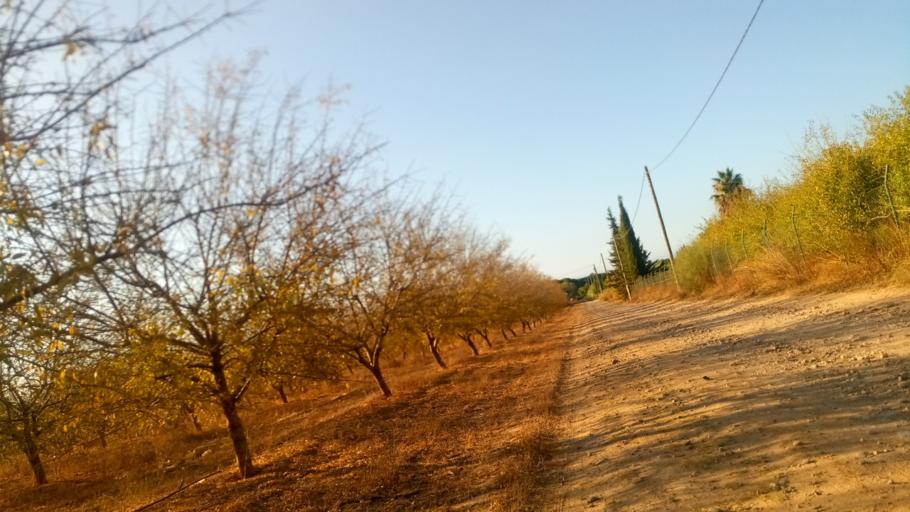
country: PT
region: Faro
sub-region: Tavira
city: Tavira
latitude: 37.1462
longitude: -7.5836
